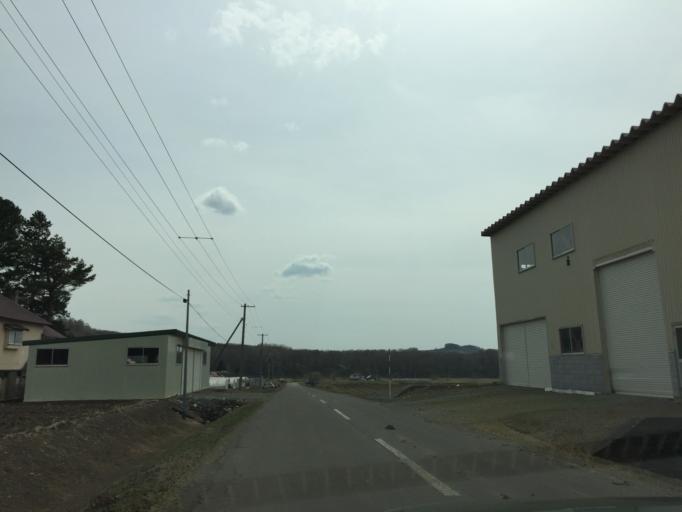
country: JP
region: Hokkaido
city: Ashibetsu
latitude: 43.6187
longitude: 142.2146
